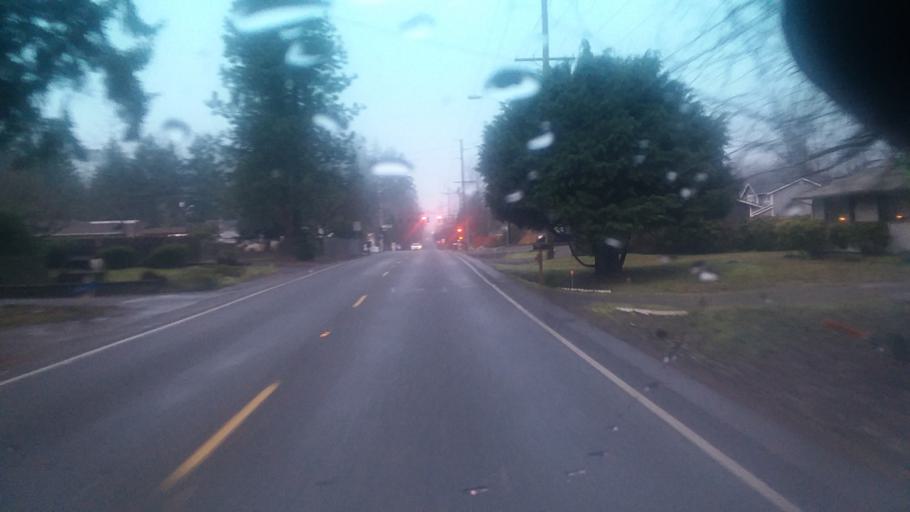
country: US
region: Washington
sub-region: Pierce County
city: South Hill
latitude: 47.1257
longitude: -122.3019
